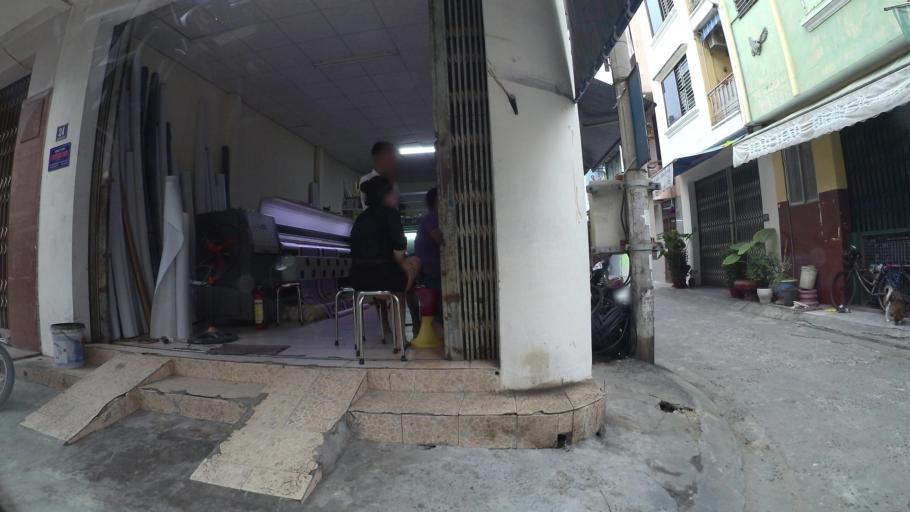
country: VN
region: Da Nang
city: Da Nang
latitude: 16.0681
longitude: 108.2128
